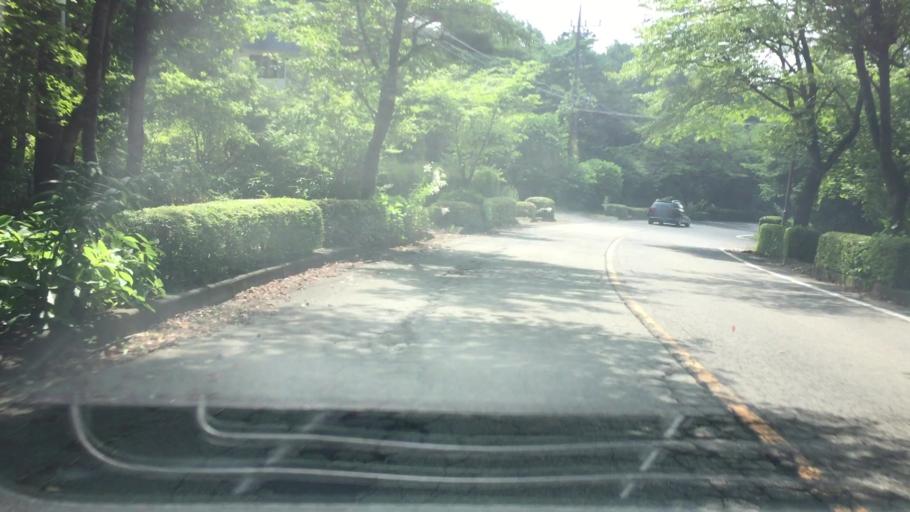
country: JP
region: Tochigi
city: Kuroiso
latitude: 37.1043
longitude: 140.0337
